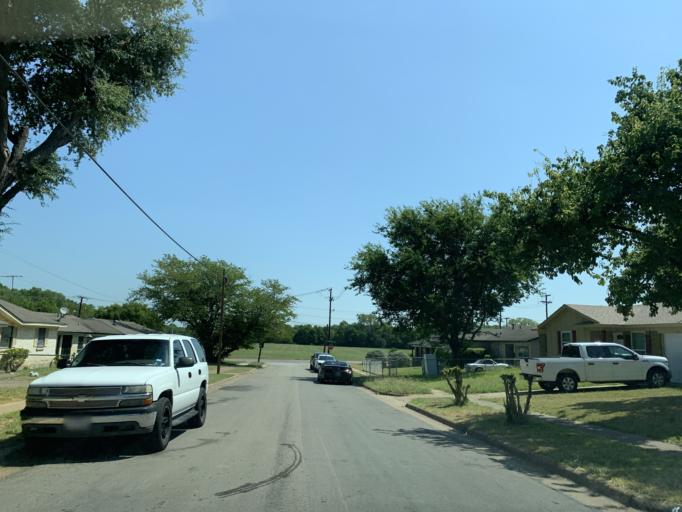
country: US
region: Texas
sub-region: Dallas County
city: Hutchins
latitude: 32.6778
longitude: -96.7511
